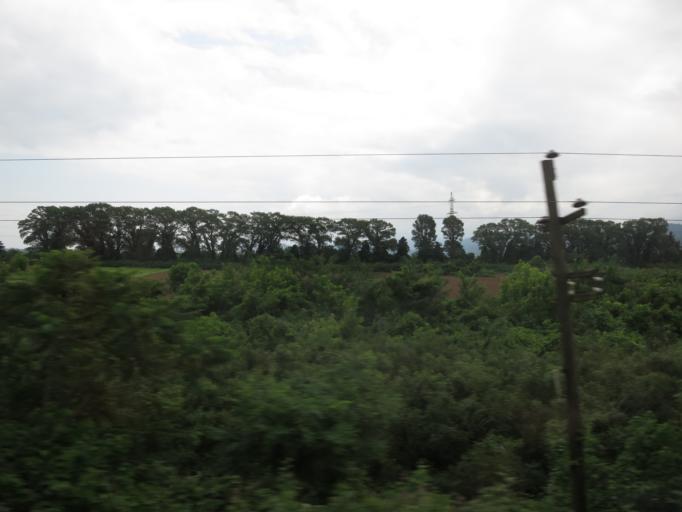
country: GE
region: Imereti
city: Samtredia
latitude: 42.1254
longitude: 42.3316
